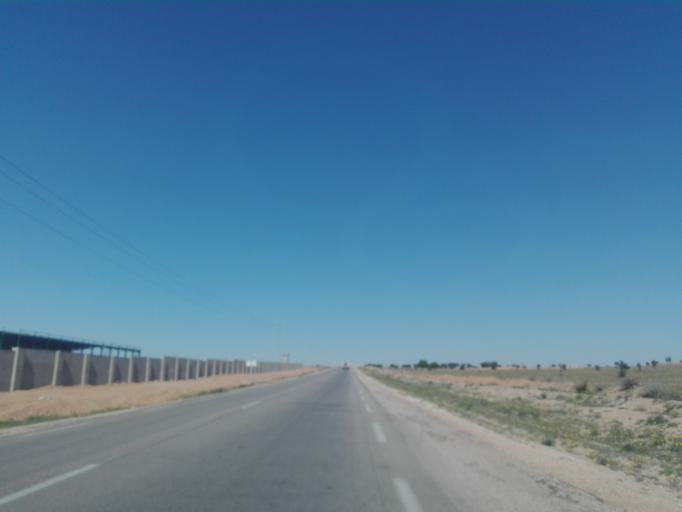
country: TN
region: Safaqis
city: Bi'r `Ali Bin Khalifah
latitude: 34.7354
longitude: 10.4141
